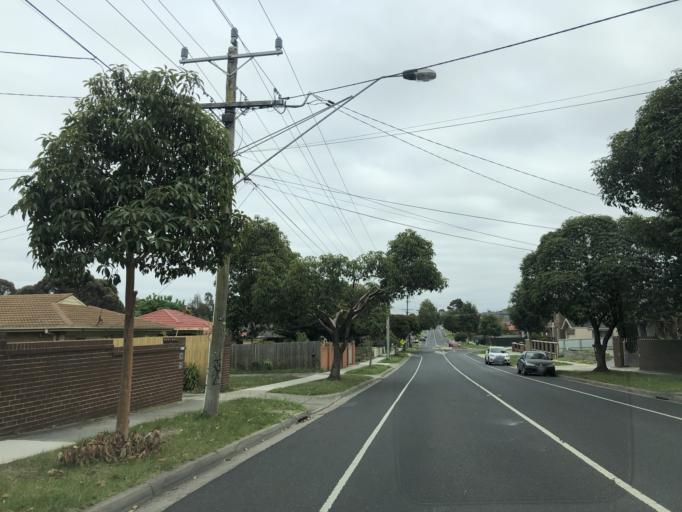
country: AU
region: Victoria
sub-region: Monash
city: Notting Hill
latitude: -37.9153
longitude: 145.1697
